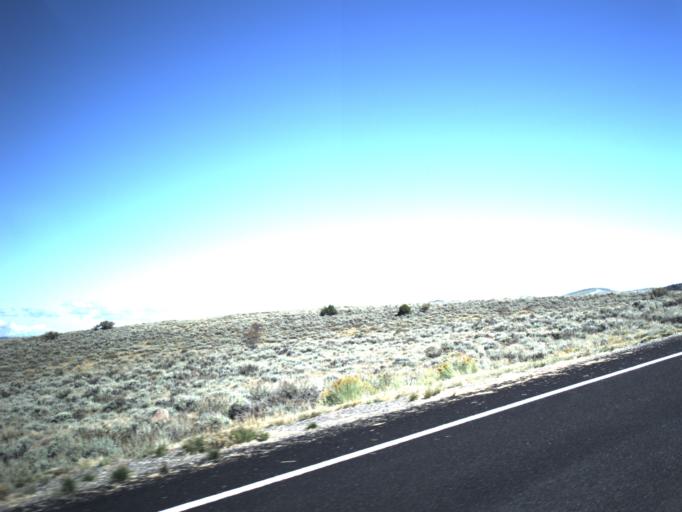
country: US
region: Utah
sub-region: Wayne County
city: Loa
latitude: 38.4964
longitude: -111.8090
